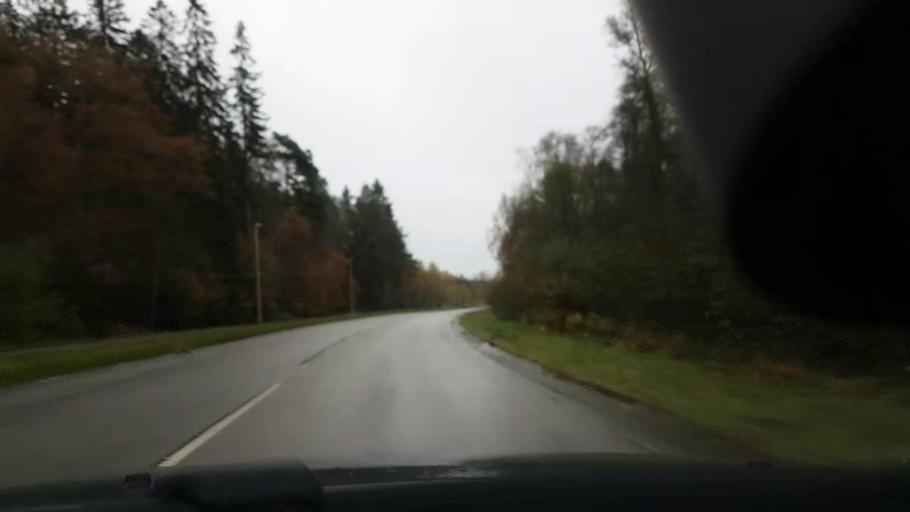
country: SE
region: Vaestra Goetaland
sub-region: Molndal
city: Kallered
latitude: 57.6002
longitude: 12.0818
